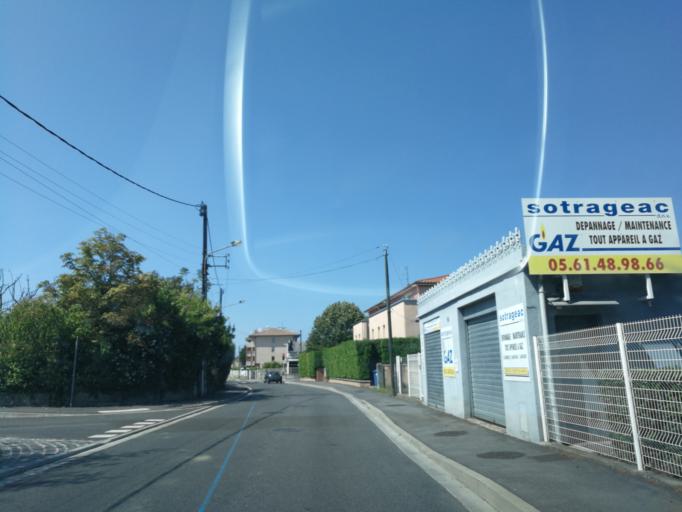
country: FR
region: Midi-Pyrenees
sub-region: Departement de la Haute-Garonne
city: L'Union
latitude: 43.6334
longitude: 1.4693
